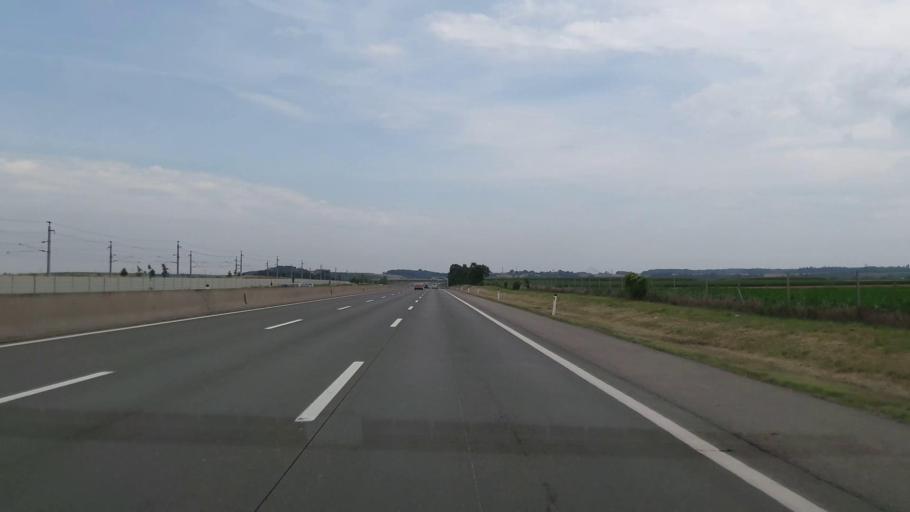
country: AT
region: Lower Austria
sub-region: Politischer Bezirk Sankt Polten
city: Sankt Margarethen an der Sierning
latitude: 48.1703
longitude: 15.5141
